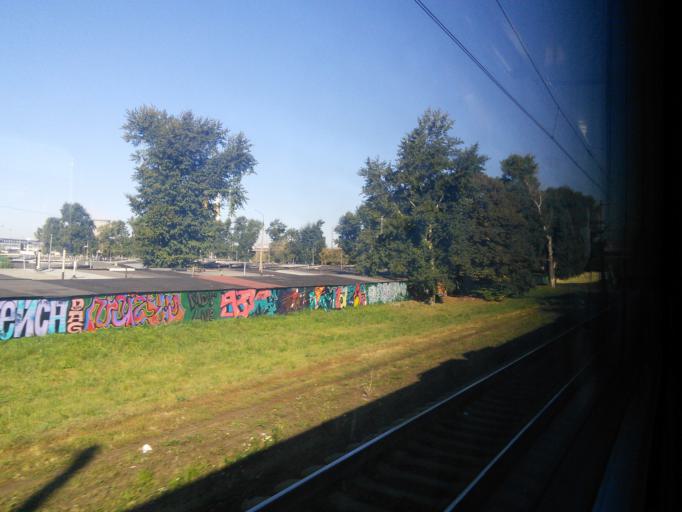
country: RU
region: Moscow
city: Tekstil'shchiki
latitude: 55.7222
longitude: 37.7168
